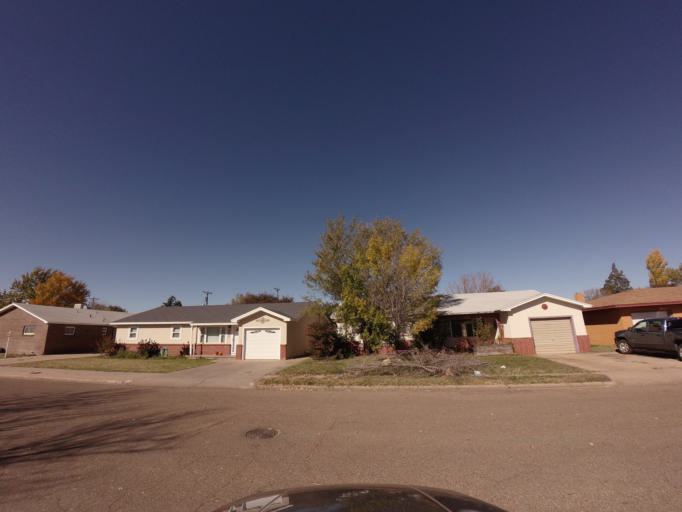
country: US
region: New Mexico
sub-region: Curry County
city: Clovis
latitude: 34.4206
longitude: -103.2041
